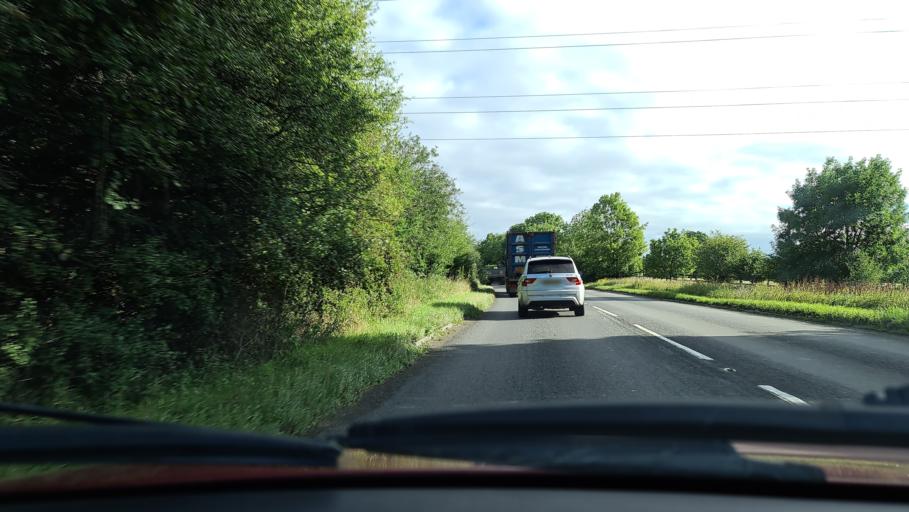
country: GB
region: England
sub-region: Buckinghamshire
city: Amersham
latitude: 51.6540
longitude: -0.6155
